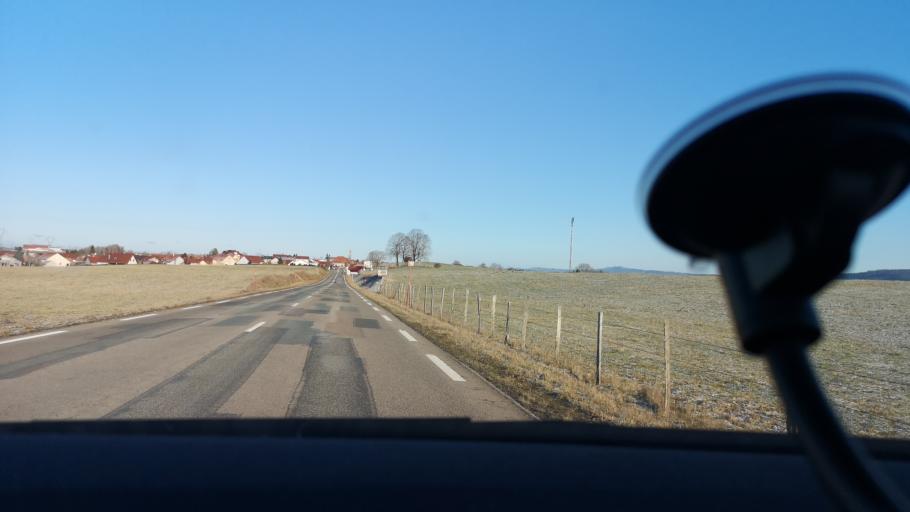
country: FR
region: Franche-Comte
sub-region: Departement du Doubs
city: Frasne
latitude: 46.8475
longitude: 6.1439
